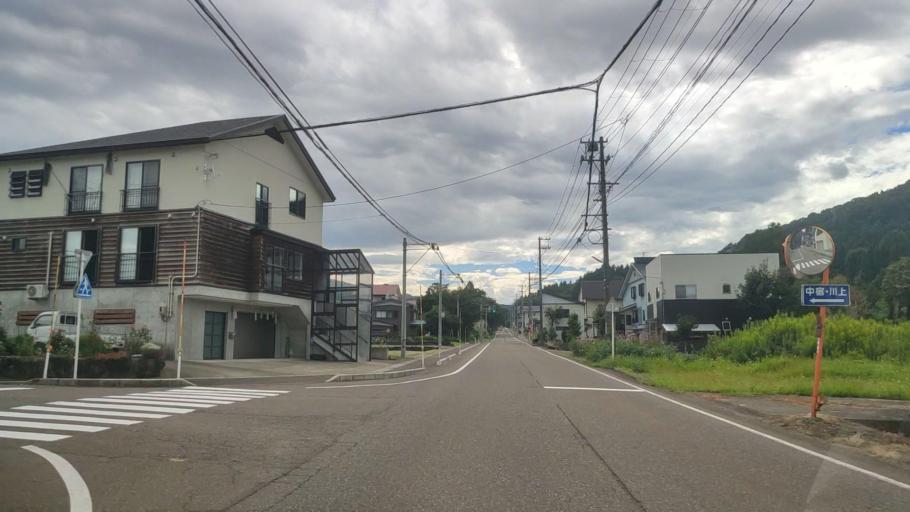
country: JP
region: Niigata
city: Arai
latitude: 37.0019
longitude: 138.2643
